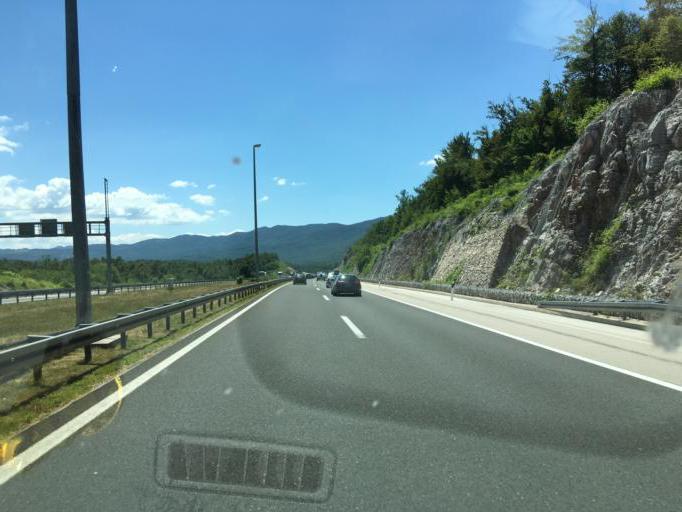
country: HR
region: Zadarska
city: Obrovac
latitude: 44.3632
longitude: 15.6389
